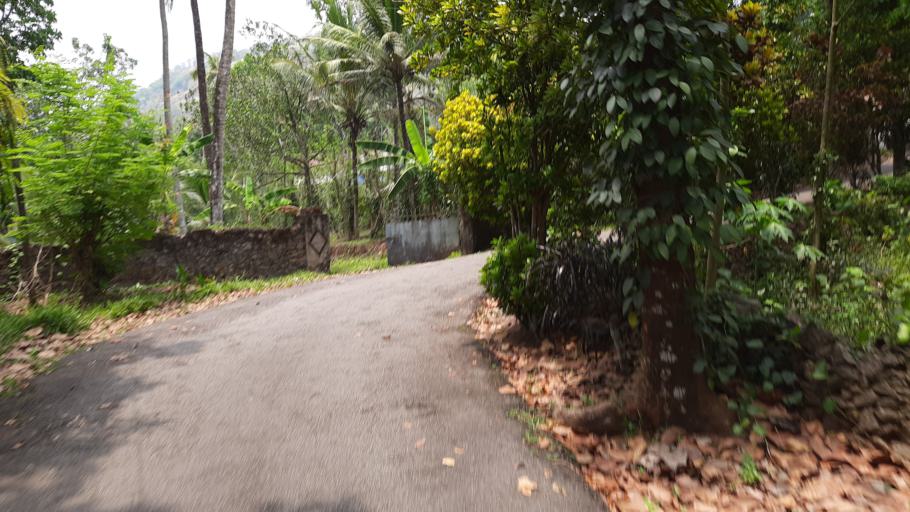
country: IN
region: Kerala
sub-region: Kottayam
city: Lalam
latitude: 9.8243
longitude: 76.7277
